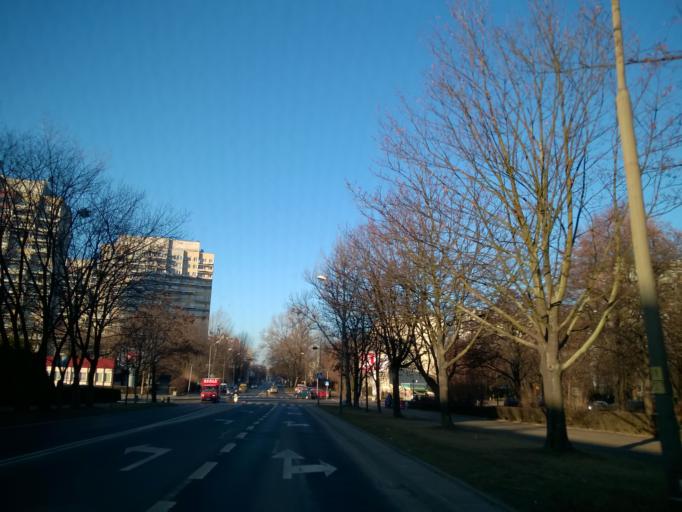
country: PL
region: Lower Silesian Voivodeship
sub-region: Powiat wroclawski
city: Wroclaw
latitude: 51.1159
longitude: 17.0133
